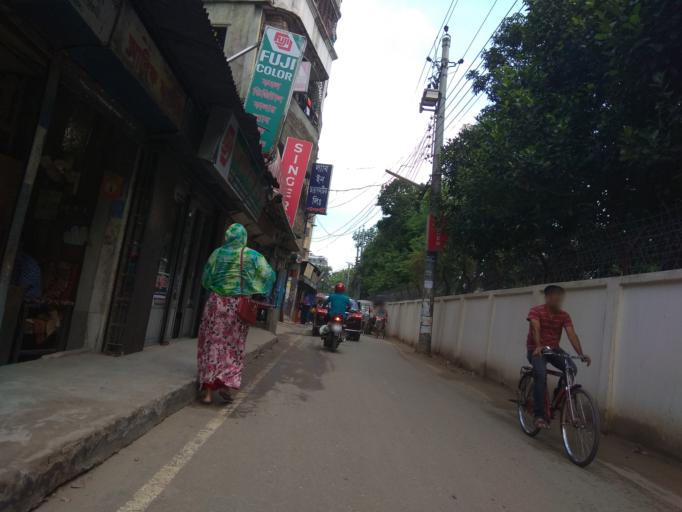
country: BD
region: Dhaka
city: Tungi
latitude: 23.8283
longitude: 90.3923
